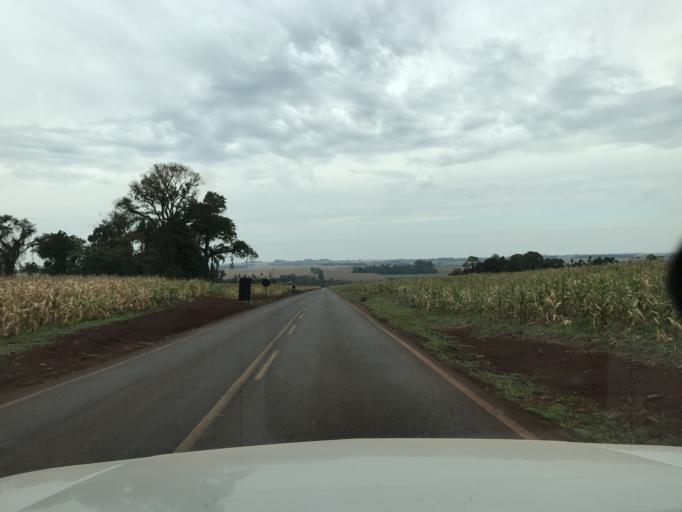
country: BR
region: Parana
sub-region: Palotina
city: Palotina
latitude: -24.4201
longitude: -53.9034
